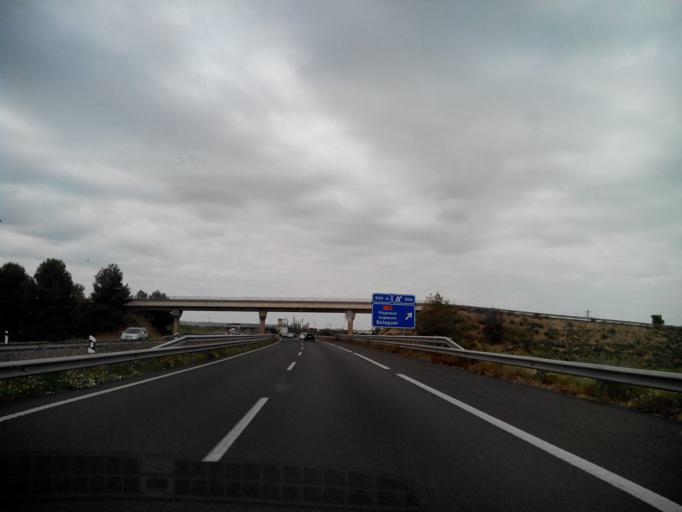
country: ES
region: Catalonia
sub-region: Provincia de Lleida
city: Anglesola
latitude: 41.6576
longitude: 1.1085
